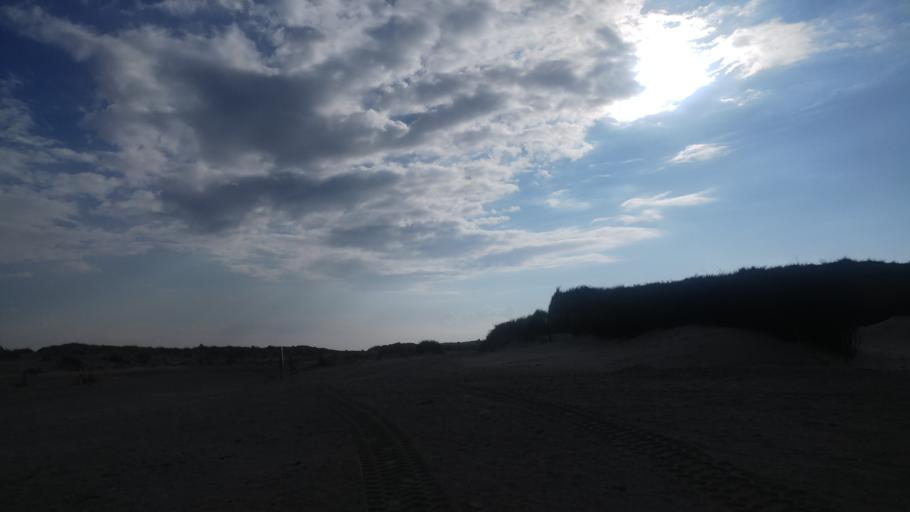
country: DE
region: Schleswig-Holstein
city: Helgoland
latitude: 54.1886
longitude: 7.9168
